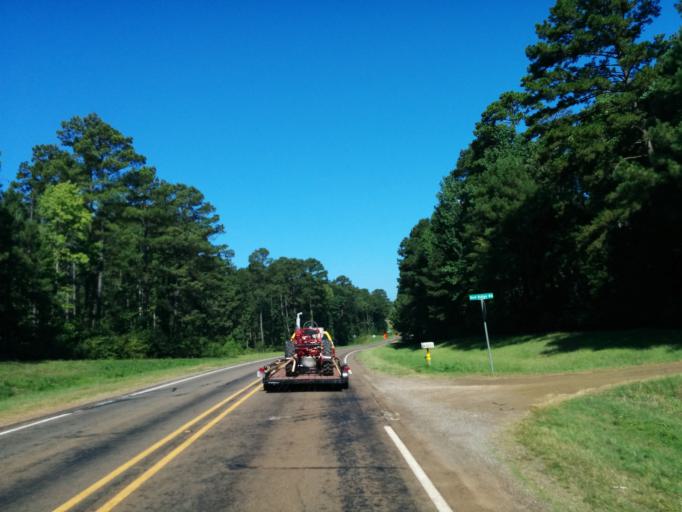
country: US
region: Texas
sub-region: Sabine County
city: Milam
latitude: 31.4292
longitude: -93.8094
